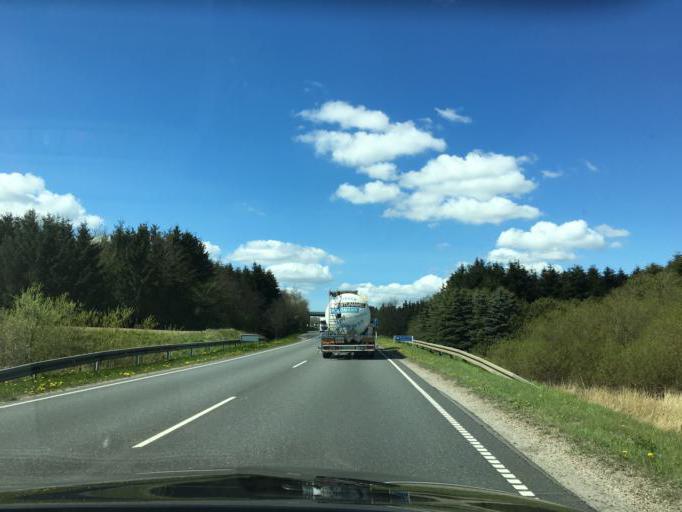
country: DK
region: Central Jutland
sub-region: Hedensted Kommune
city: Hedensted
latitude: 55.8429
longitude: 9.7453
